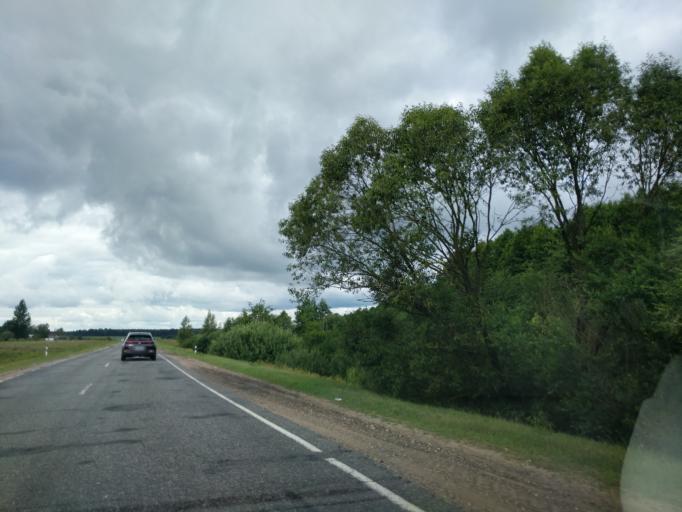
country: BY
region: Minsk
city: Il'ya
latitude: 54.4743
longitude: 27.2671
